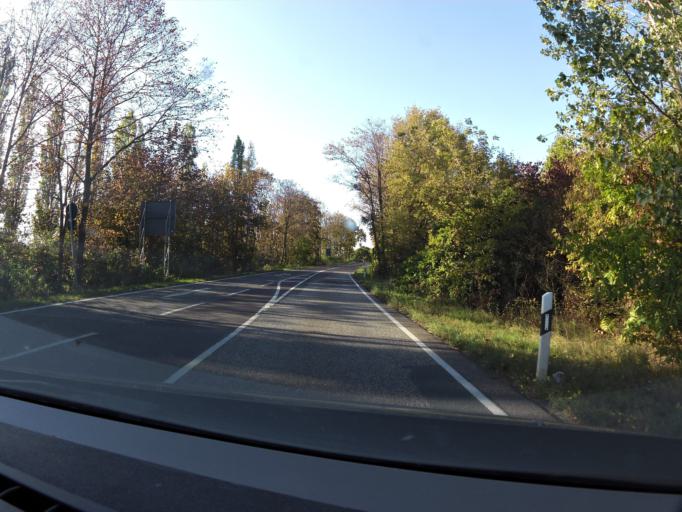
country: DE
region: Saxony-Anhalt
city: Diesdorf
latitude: 52.0731
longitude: 11.5696
